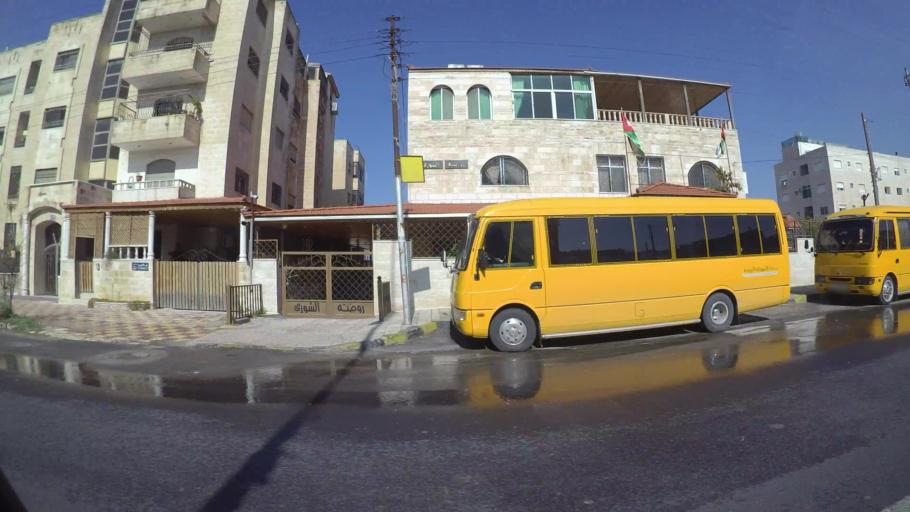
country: JO
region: Amman
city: Al Bunayyat ash Shamaliyah
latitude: 31.9247
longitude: 35.8984
